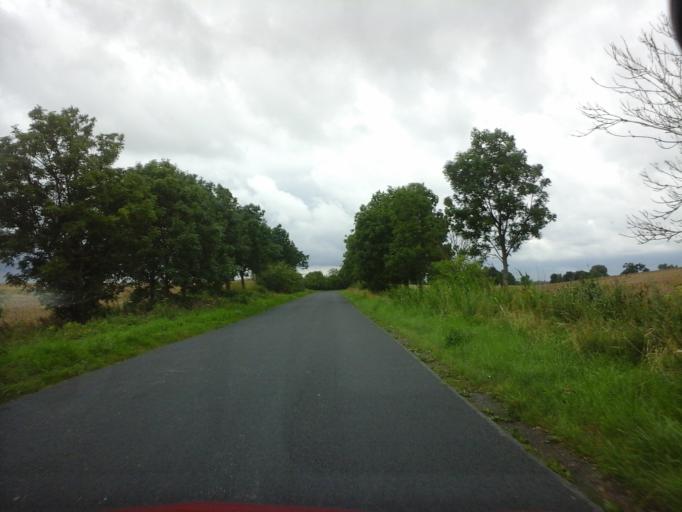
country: PL
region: West Pomeranian Voivodeship
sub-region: Powiat choszczenski
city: Bierzwnik
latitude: 53.0445
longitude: 15.6933
